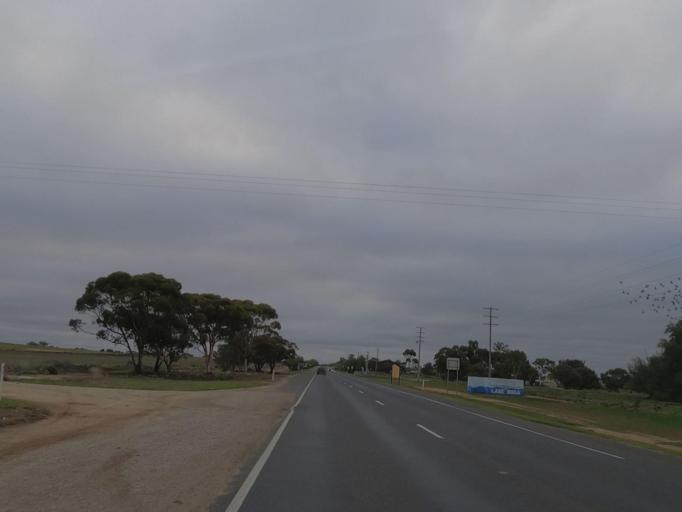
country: AU
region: Victoria
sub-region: Swan Hill
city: Swan Hill
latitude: -35.4514
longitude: 143.6250
